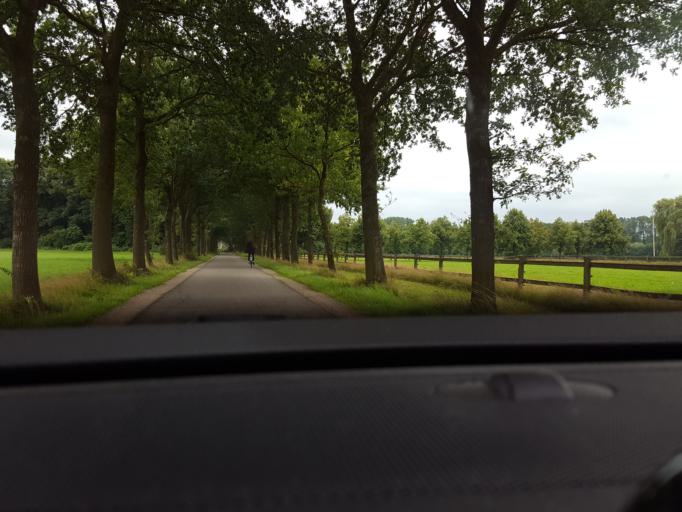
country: NL
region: Gelderland
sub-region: Gemeente Lochem
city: Almen
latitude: 52.1138
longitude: 6.2803
